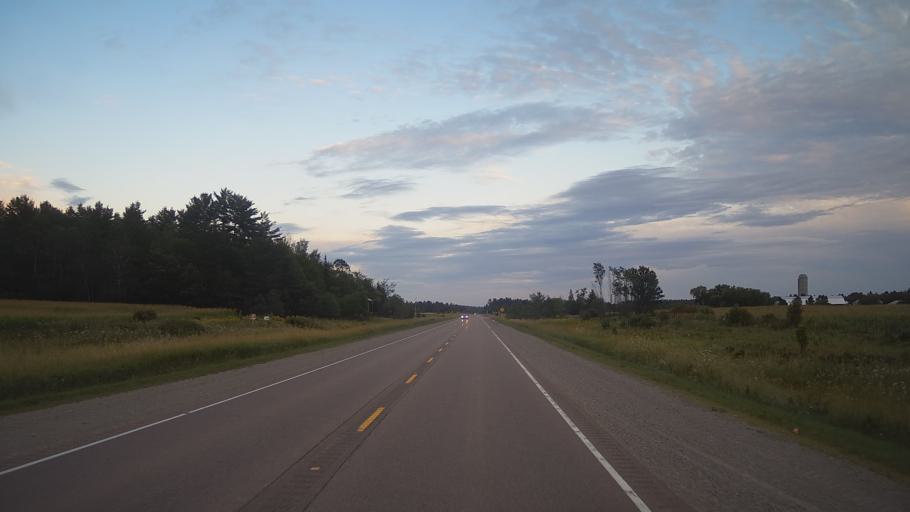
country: CA
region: Ontario
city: Pembroke
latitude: 45.7875
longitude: -77.1060
